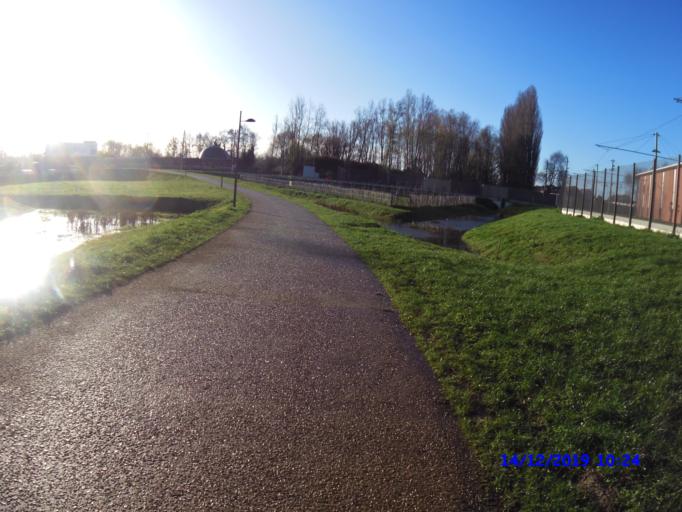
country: BE
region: Flanders
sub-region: Provincie Vlaams-Brabant
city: Drogenbos
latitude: 50.7981
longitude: 4.3154
